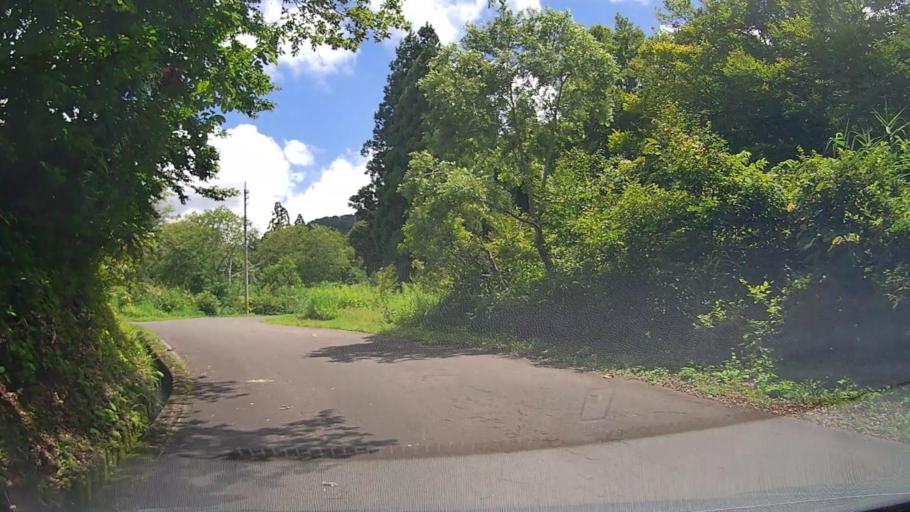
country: JP
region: Nagano
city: Iiyama
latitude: 36.9315
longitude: 138.4691
